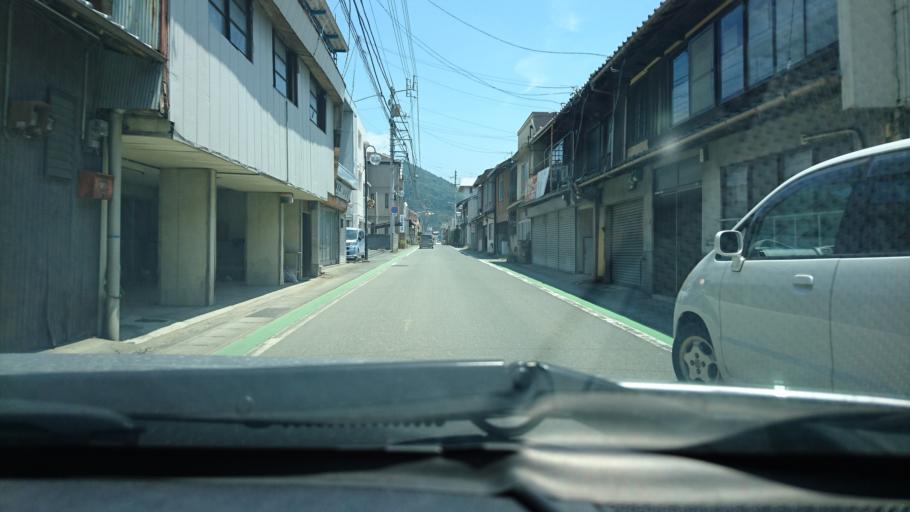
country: JP
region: Ehime
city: Ozu
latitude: 33.5076
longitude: 132.5395
